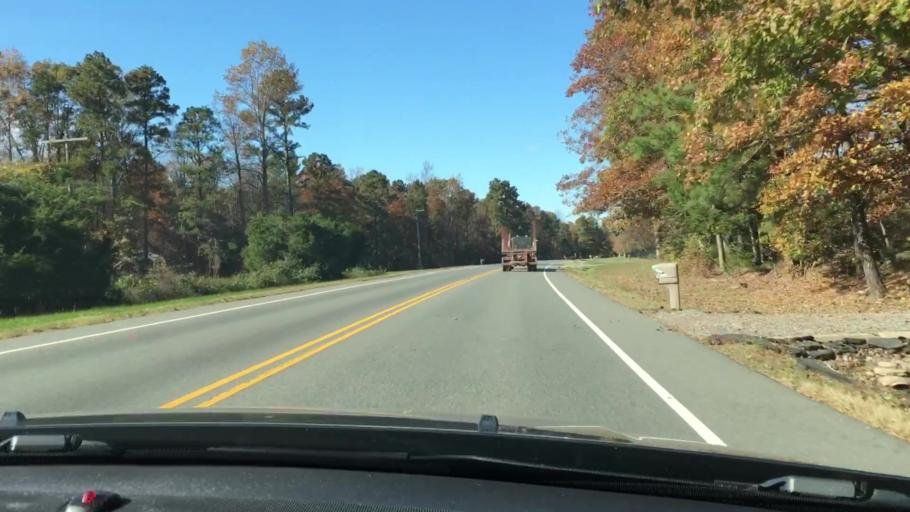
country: US
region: Virginia
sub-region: King William County
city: Central Garage
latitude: 37.7792
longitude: -77.1659
